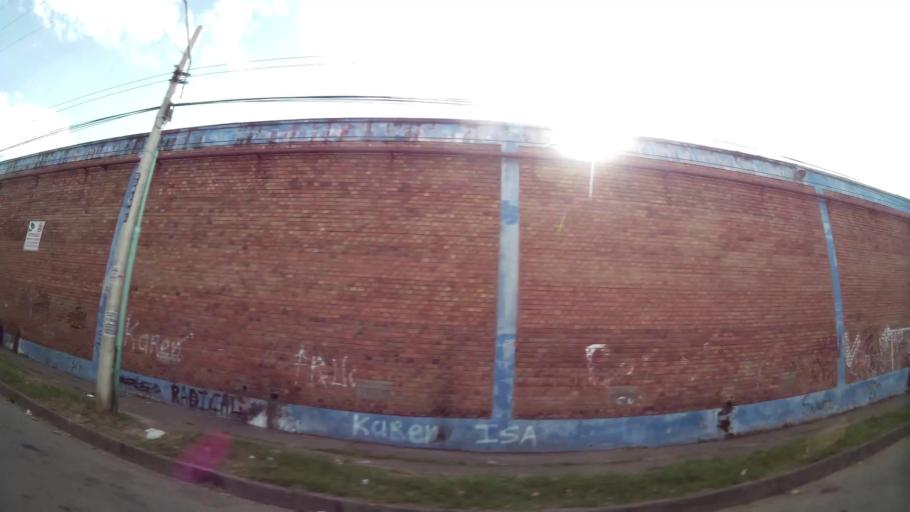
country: CO
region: Valle del Cauca
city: Cali
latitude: 3.4688
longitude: -76.5142
